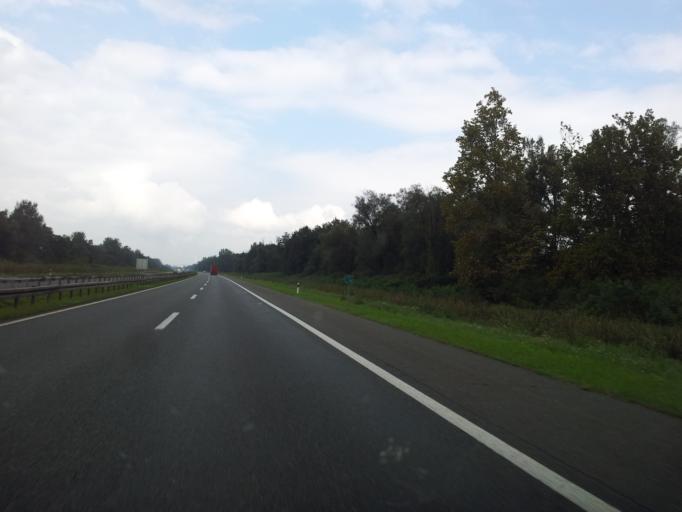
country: HR
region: Sisacko-Moslavacka
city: Lipovljani
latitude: 45.4136
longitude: 16.8516
